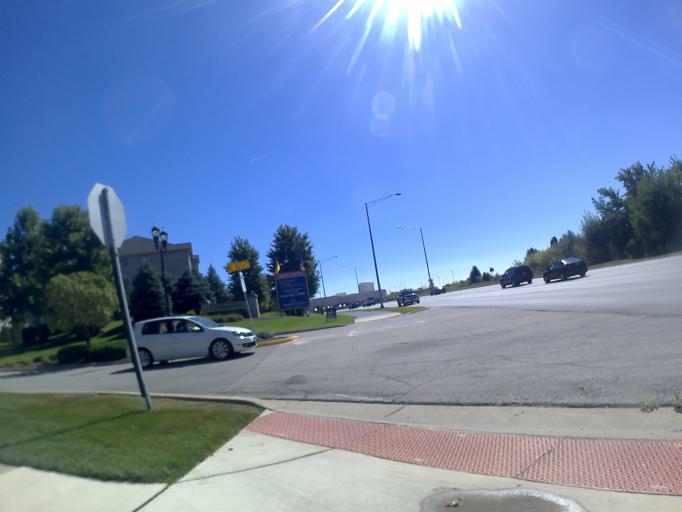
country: US
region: Illinois
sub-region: DuPage County
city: Woodridge
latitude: 41.7311
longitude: -88.0303
